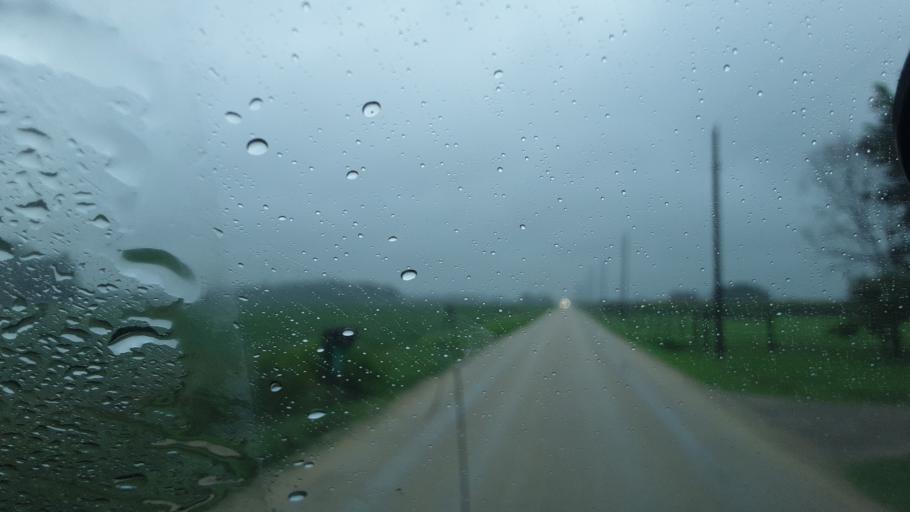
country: US
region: Indiana
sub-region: Adams County
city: Berne
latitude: 40.6876
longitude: -84.9237
